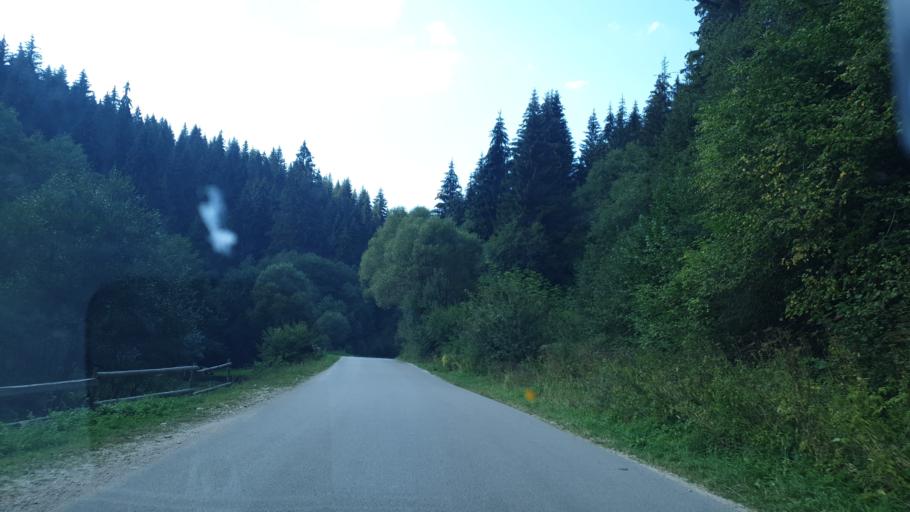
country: RS
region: Central Serbia
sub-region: Zlatiborski Okrug
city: Nova Varos
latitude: 43.4437
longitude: 19.8520
